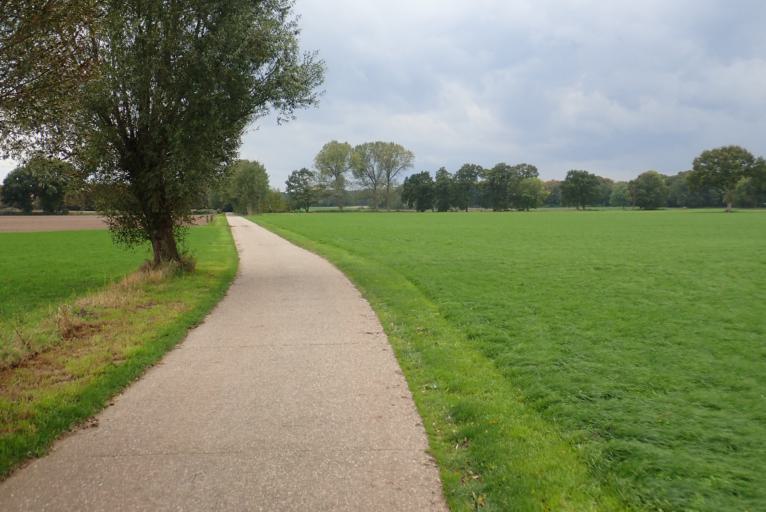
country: BE
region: Flanders
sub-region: Provincie Antwerpen
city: Kalmthout
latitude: 51.4132
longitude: 4.4829
